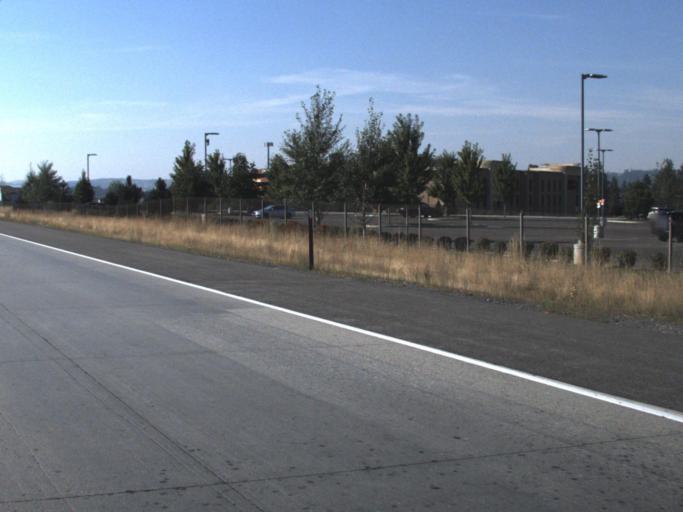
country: US
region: Washington
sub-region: Spokane County
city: Veradale
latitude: 47.6664
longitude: -117.1823
